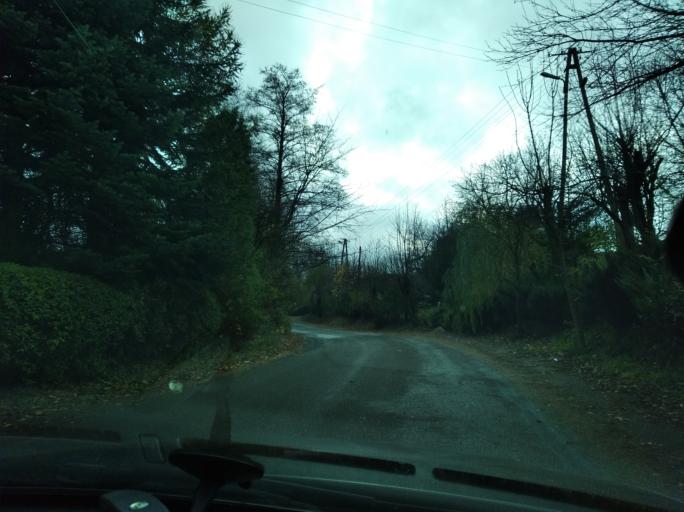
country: PL
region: Subcarpathian Voivodeship
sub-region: Powiat przeworski
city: Sietesz
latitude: 49.9773
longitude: 22.3412
